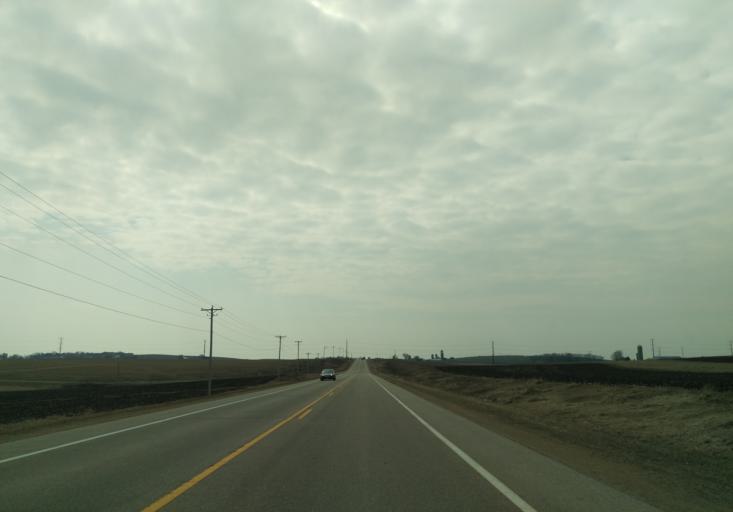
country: US
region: Wisconsin
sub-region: Columbia County
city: Lodi
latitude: 43.2670
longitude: -89.5212
